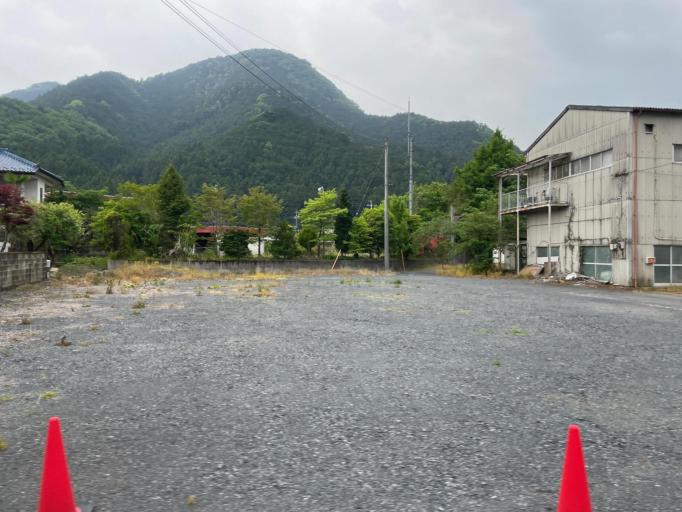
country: JP
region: Tochigi
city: Tanuma
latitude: 36.4513
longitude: 139.6401
